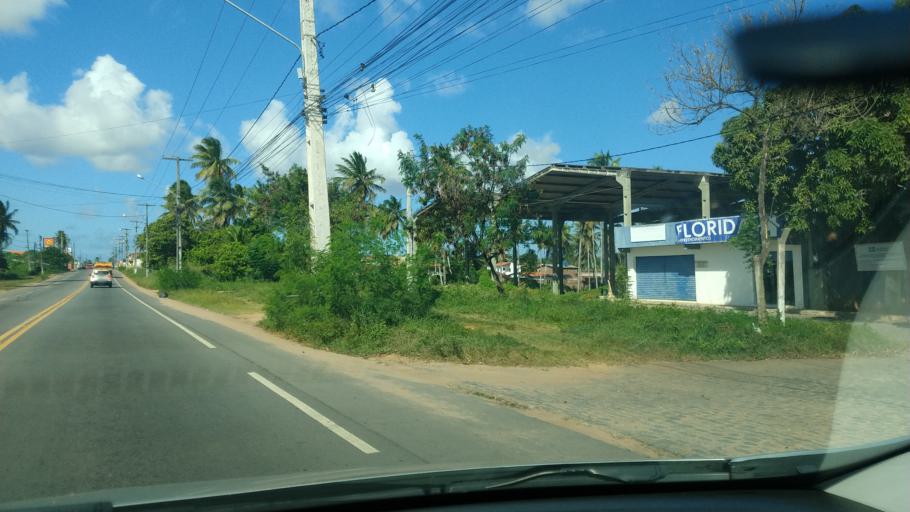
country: BR
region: Rio Grande do Norte
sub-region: Sao Goncalo Do Amarante
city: Sao Goncalo do Amarante
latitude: -5.7889
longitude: -35.3021
